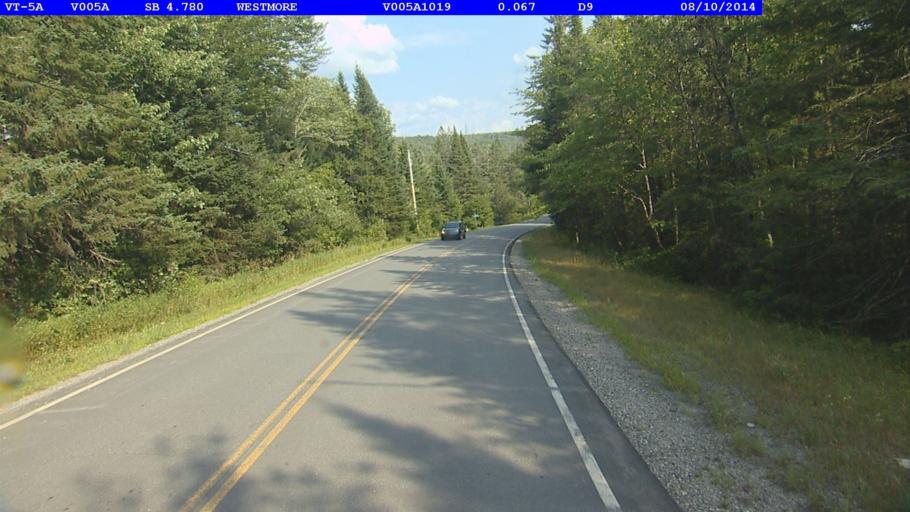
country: US
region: Vermont
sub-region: Caledonia County
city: Lyndonville
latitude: 44.7036
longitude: -72.0082
